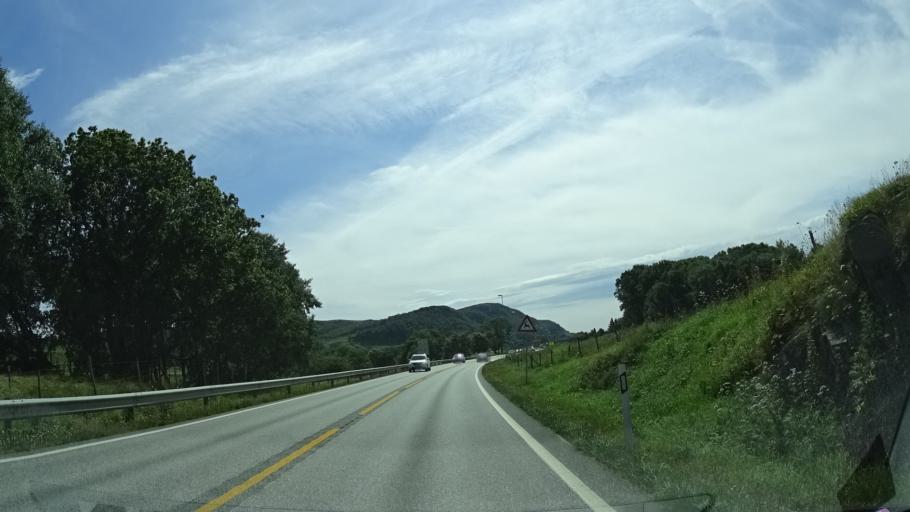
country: NO
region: Rogaland
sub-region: Rennesoy
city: Vikevag
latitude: 59.1170
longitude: 5.6966
